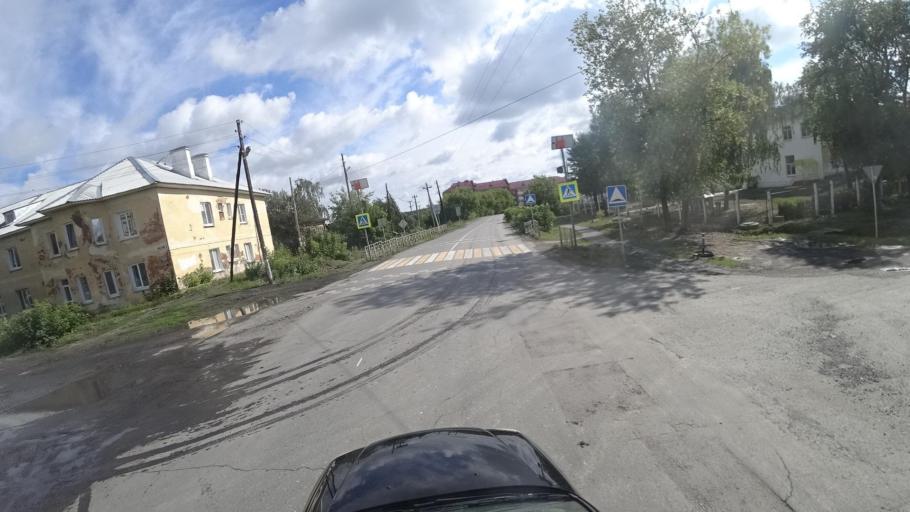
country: RU
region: Sverdlovsk
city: Kamyshlov
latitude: 56.8471
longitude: 62.6916
